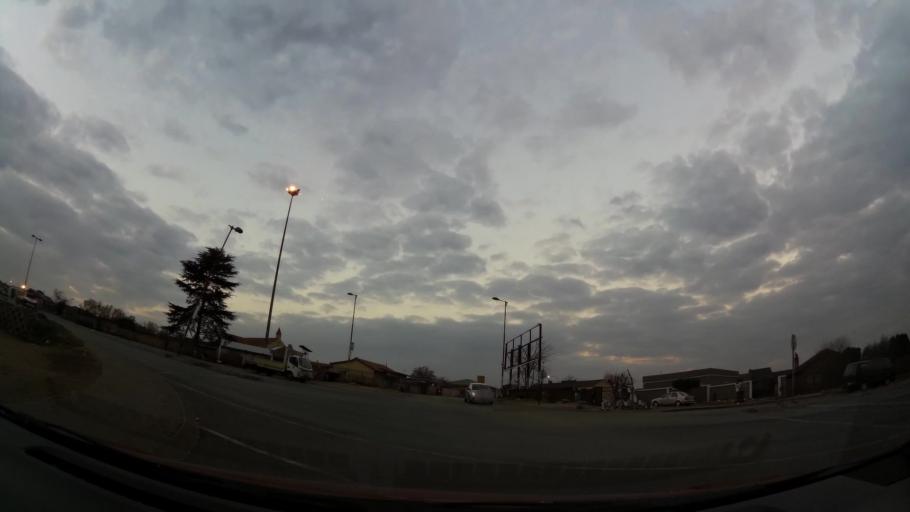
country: ZA
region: Gauteng
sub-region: City of Johannesburg Metropolitan Municipality
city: Soweto
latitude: -26.2489
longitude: 27.9259
